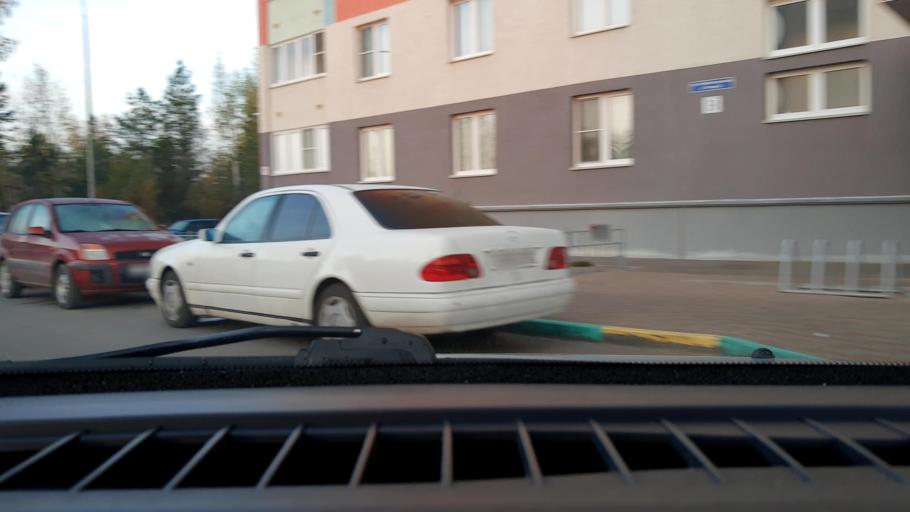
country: RU
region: Nizjnij Novgorod
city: Gorbatovka
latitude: 56.3613
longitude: 43.7976
